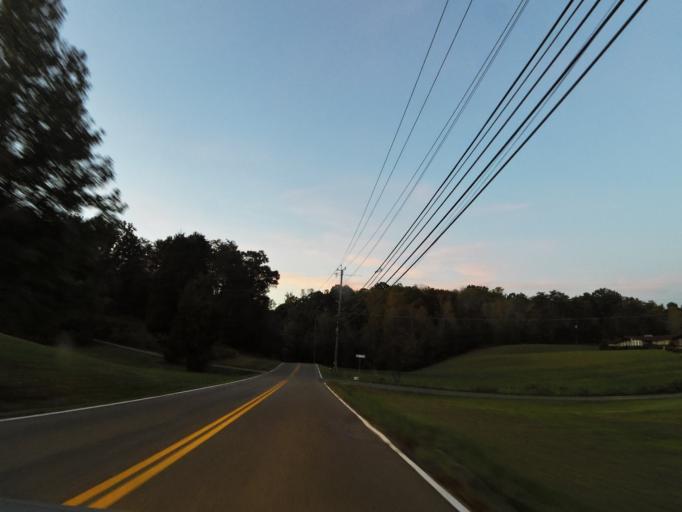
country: US
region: Tennessee
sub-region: Knox County
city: Mascot
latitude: 36.0021
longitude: -83.6370
